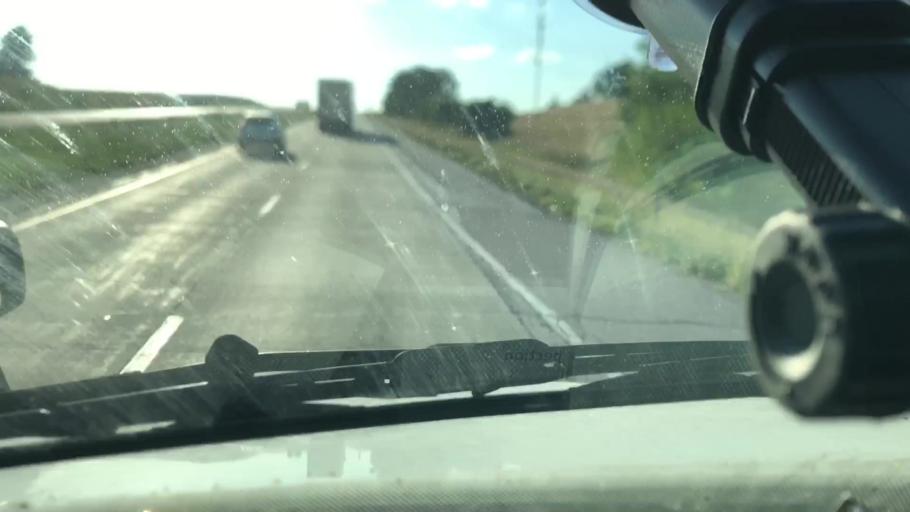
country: US
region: Iowa
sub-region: Pottawattamie County
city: Avoca
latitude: 41.4990
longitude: -95.4584
